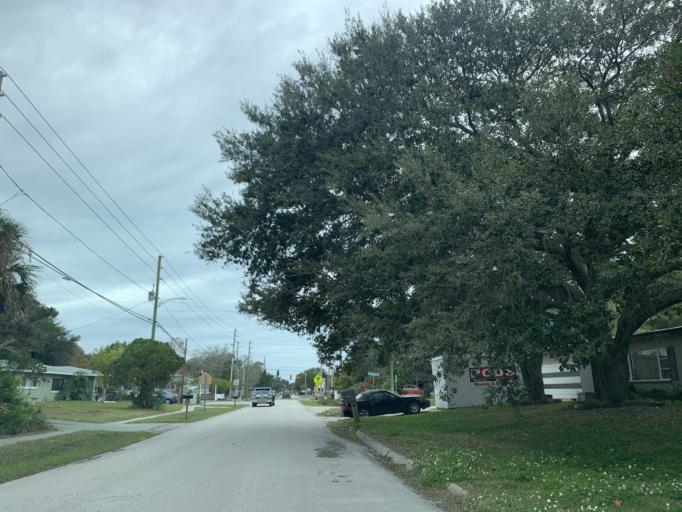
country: US
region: Florida
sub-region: Pinellas County
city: Belleair
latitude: 27.9352
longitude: -82.7859
